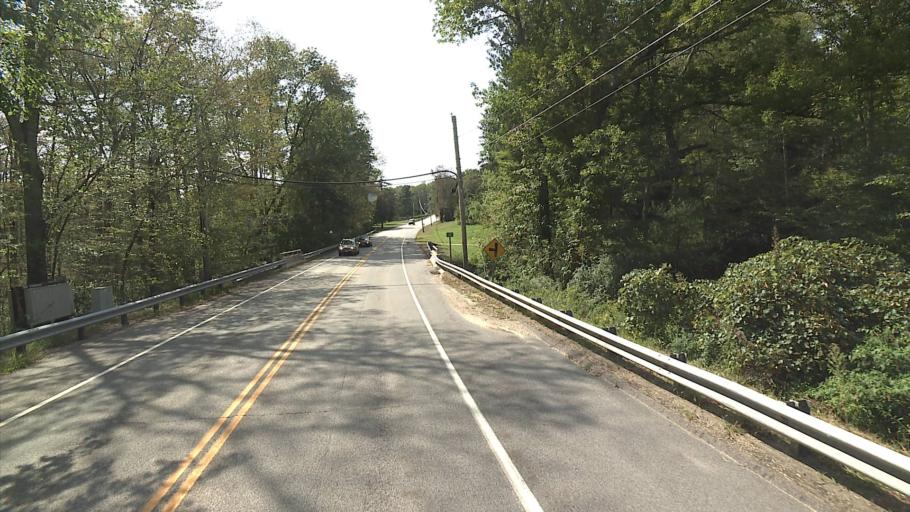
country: US
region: Connecticut
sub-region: Windham County
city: Wauregan
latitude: 41.7425
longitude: -71.9602
